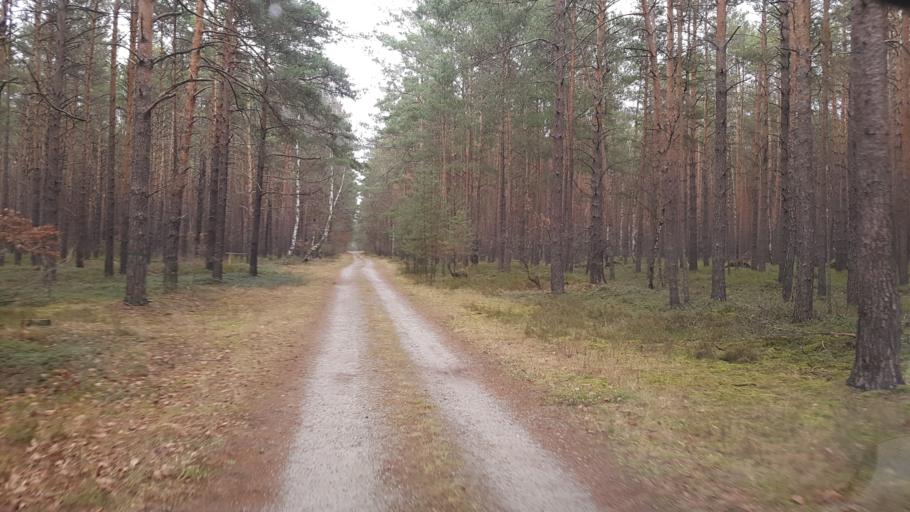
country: DE
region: Brandenburg
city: Finsterwalde
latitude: 51.6123
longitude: 13.7740
